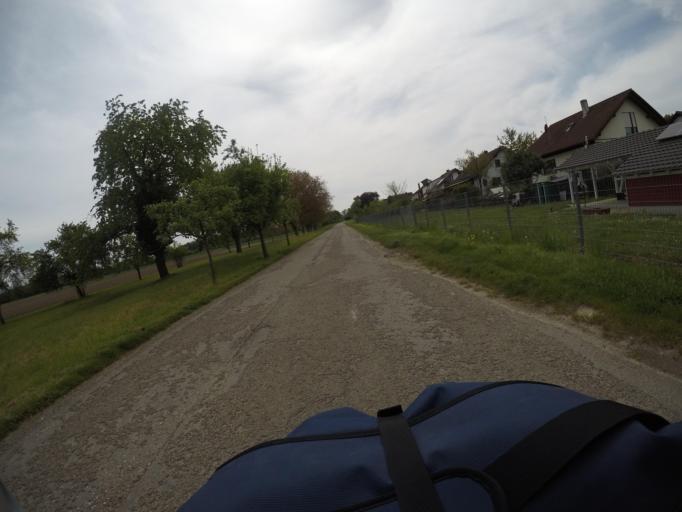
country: DE
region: Baden-Wuerttemberg
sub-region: Freiburg Region
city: Kehl
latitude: 48.6027
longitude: 7.8425
